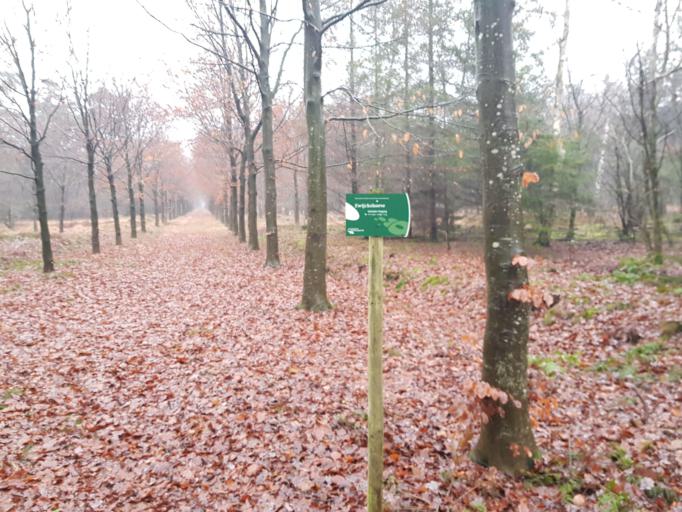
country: NL
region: Utrecht
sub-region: Gemeente Soest
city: Soest
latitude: 52.1583
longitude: 5.2467
